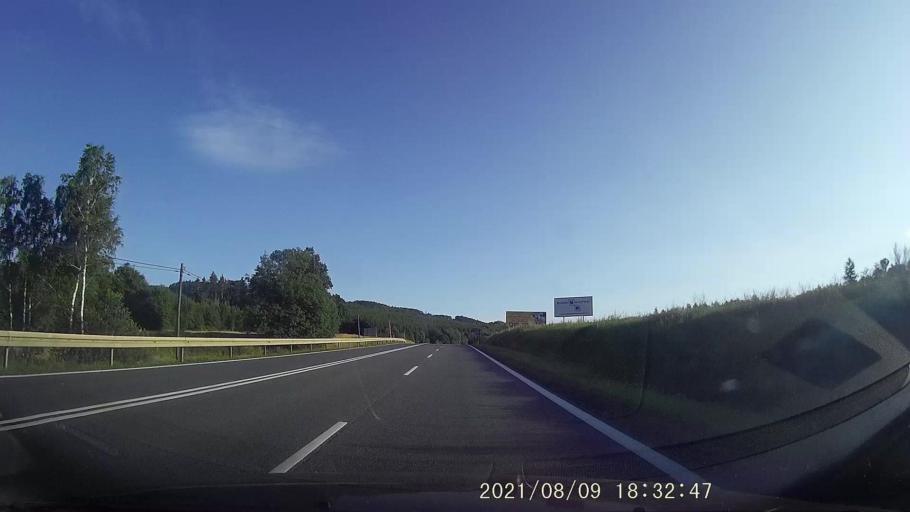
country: PL
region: Lower Silesian Voivodeship
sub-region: Powiat zabkowicki
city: Bardo
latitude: 50.4950
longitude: 16.7261
